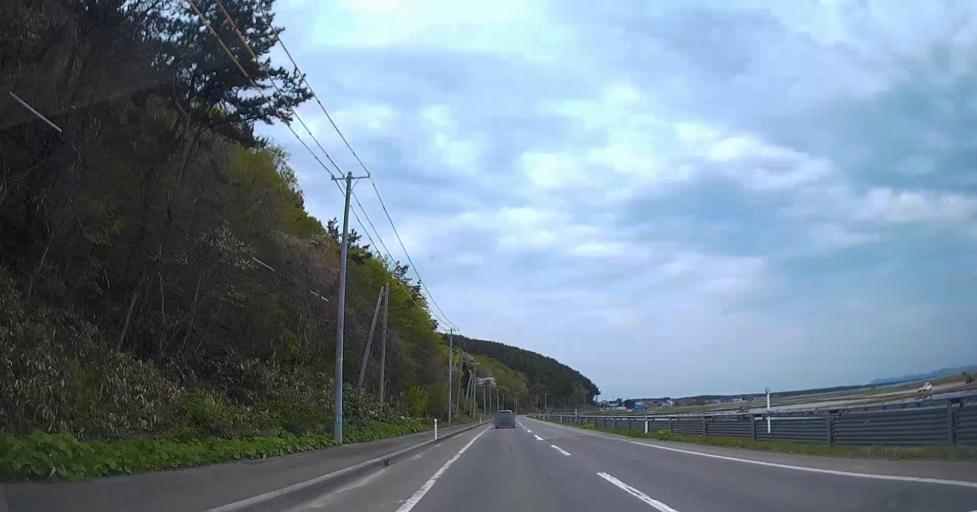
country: JP
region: Aomori
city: Shimokizukuri
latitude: 40.9954
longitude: 140.3519
